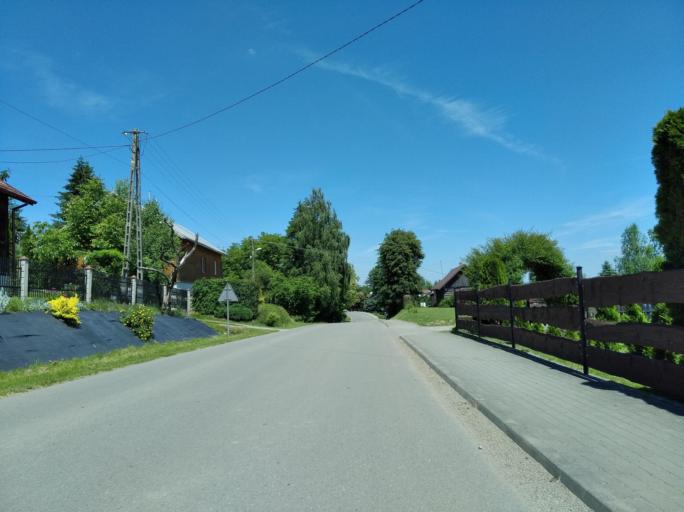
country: PL
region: Subcarpathian Voivodeship
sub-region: Powiat jasielski
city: Tarnowiec
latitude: 49.7117
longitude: 21.5540
